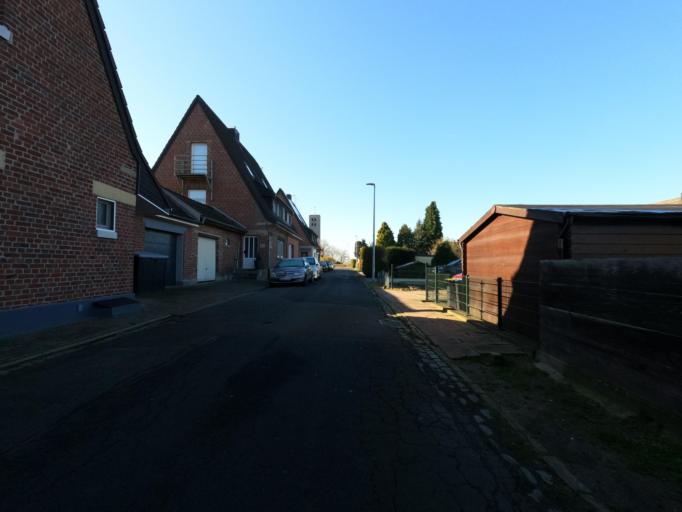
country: DE
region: North Rhine-Westphalia
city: Huckelhoven
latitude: 51.0595
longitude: 6.2231
